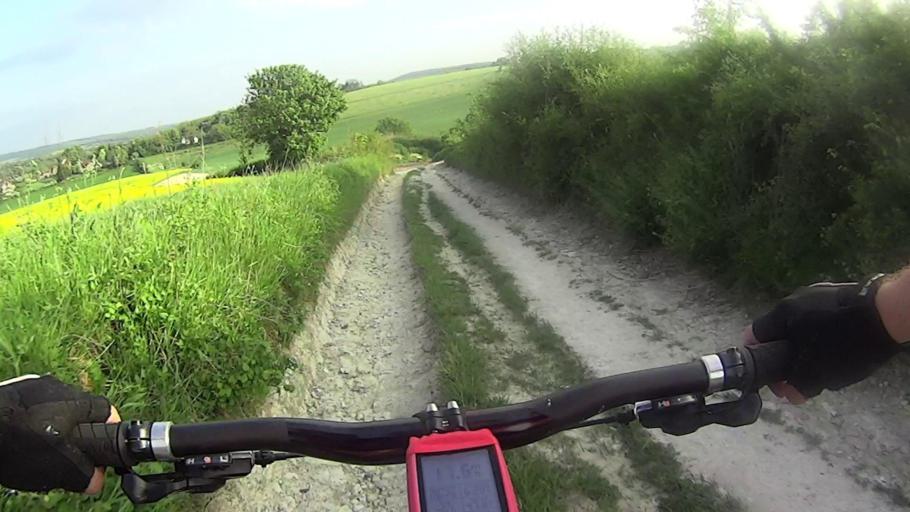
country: GB
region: England
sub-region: West Sussex
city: Arundel
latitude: 50.8977
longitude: -0.5601
